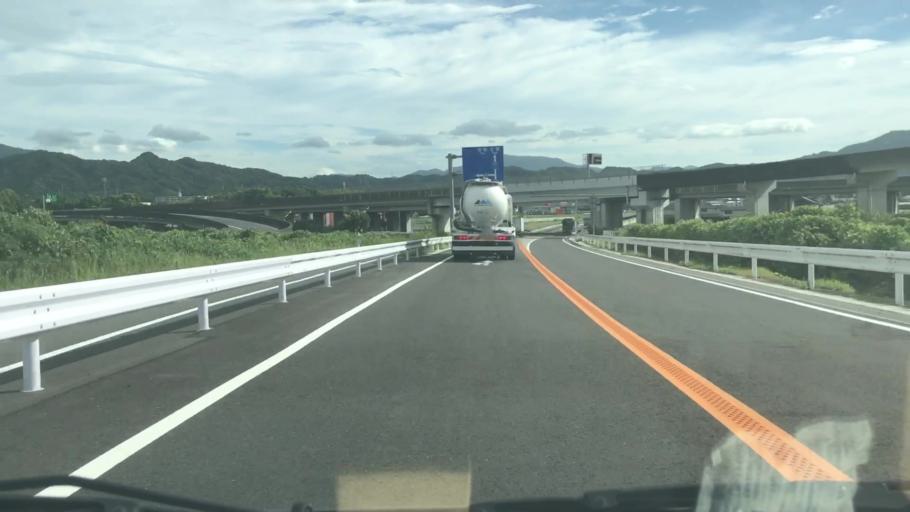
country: JP
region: Saga Prefecture
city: Takeocho-takeo
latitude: 33.2129
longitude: 130.0505
